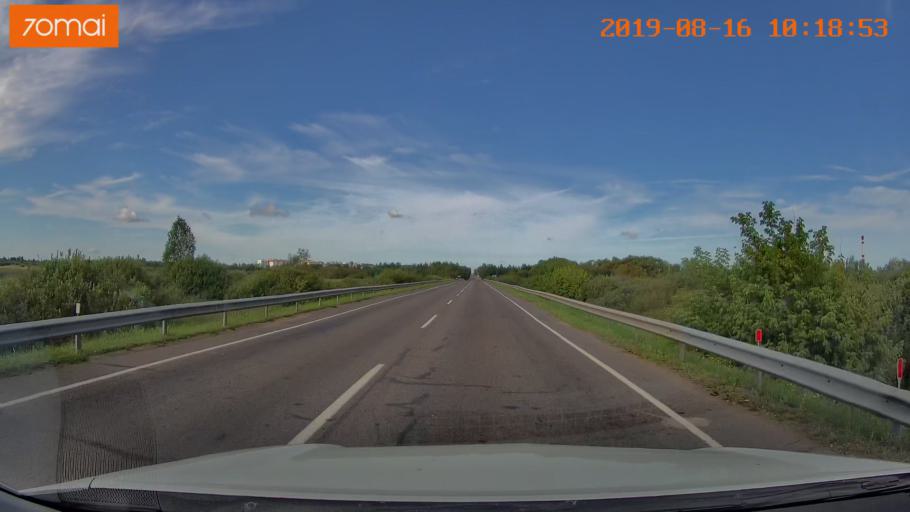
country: BY
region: Mogilev
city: Asipovichy
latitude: 53.3061
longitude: 28.6795
